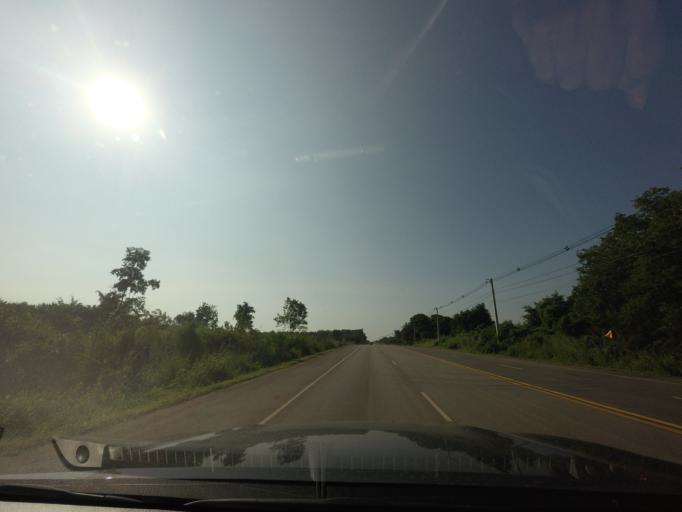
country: TH
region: Phetchabun
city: Lom Kao
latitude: 16.8551
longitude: 101.1739
